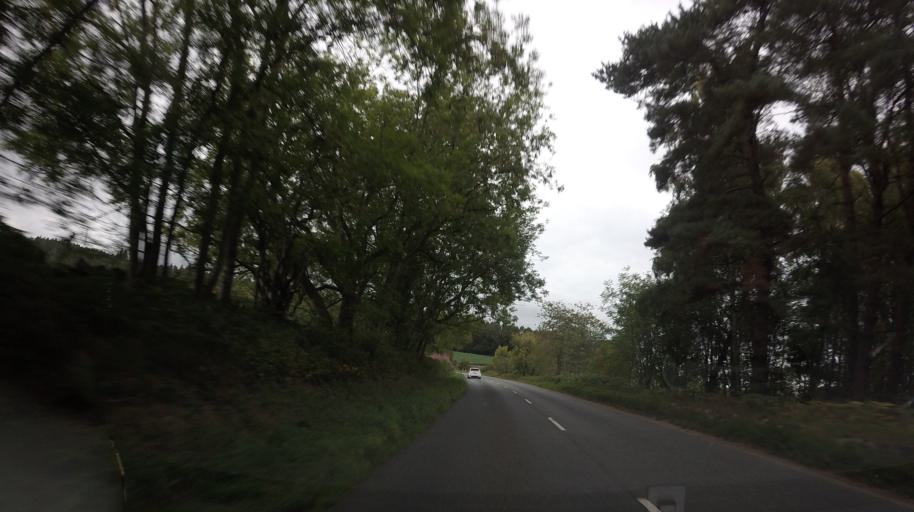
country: GB
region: Scotland
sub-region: Aberdeenshire
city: Banchory
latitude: 57.1172
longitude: -2.4263
